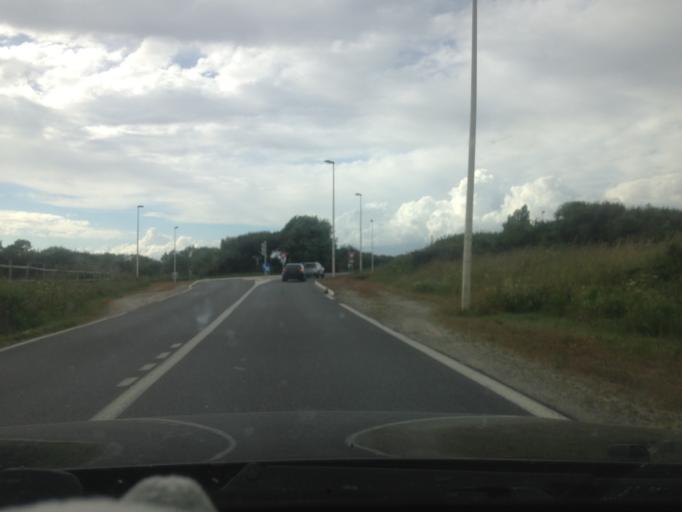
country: FR
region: Brittany
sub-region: Departement du Morbihan
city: Plouharnel
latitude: 47.6196
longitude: -3.1343
